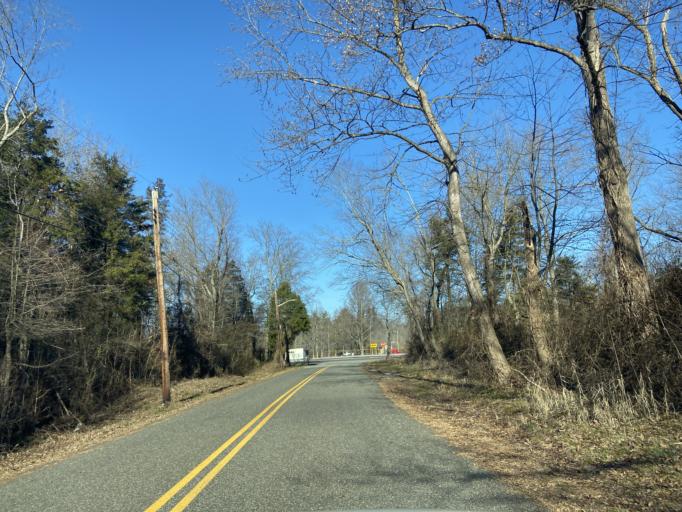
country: US
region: New Jersey
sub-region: Cumberland County
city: Vineland
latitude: 39.4948
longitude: -75.0751
